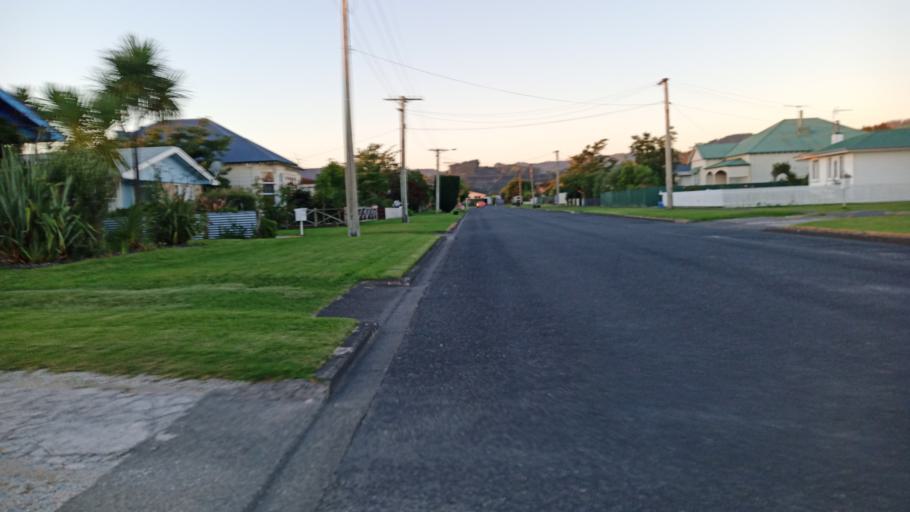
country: NZ
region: Gisborne
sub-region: Gisborne District
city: Gisborne
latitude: -38.6516
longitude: 178.0039
